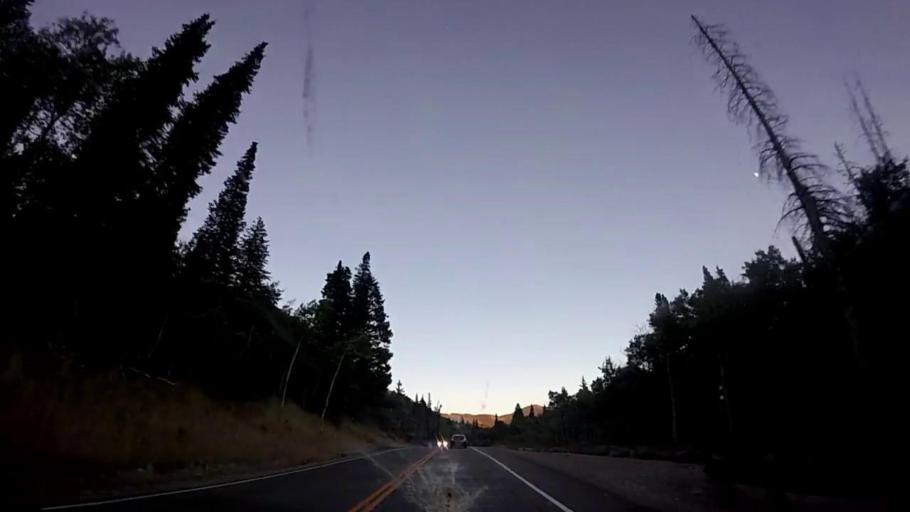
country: US
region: Utah
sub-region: Summit County
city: Snyderville
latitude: 40.6377
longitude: -111.6207
